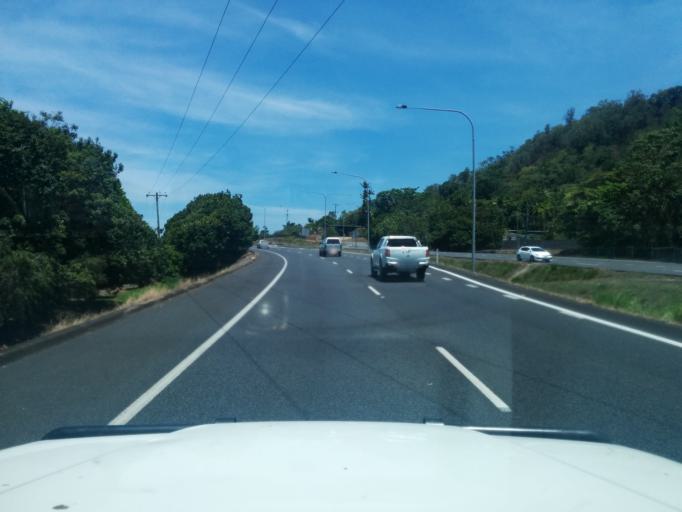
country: AU
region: Queensland
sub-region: Cairns
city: Redlynch
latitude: -16.9085
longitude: 145.7126
